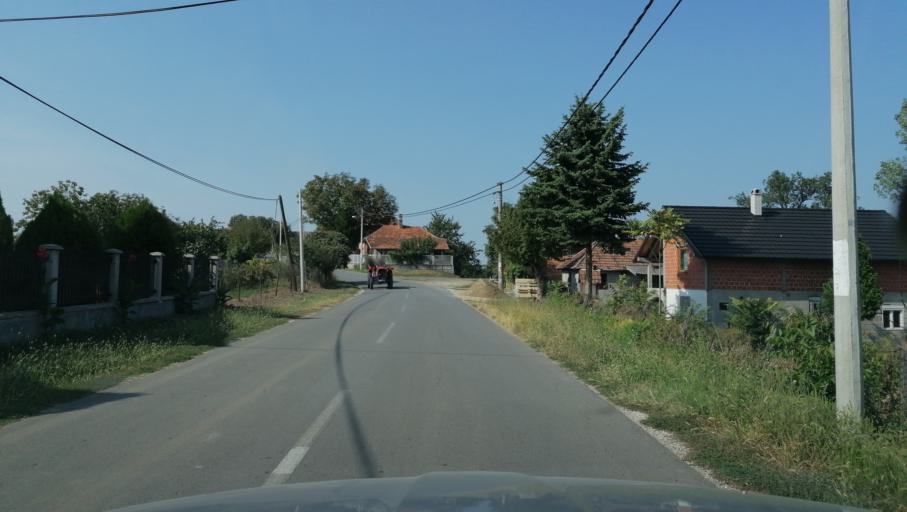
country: RS
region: Central Serbia
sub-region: Belgrade
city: Sopot
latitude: 44.5994
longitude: 20.6059
